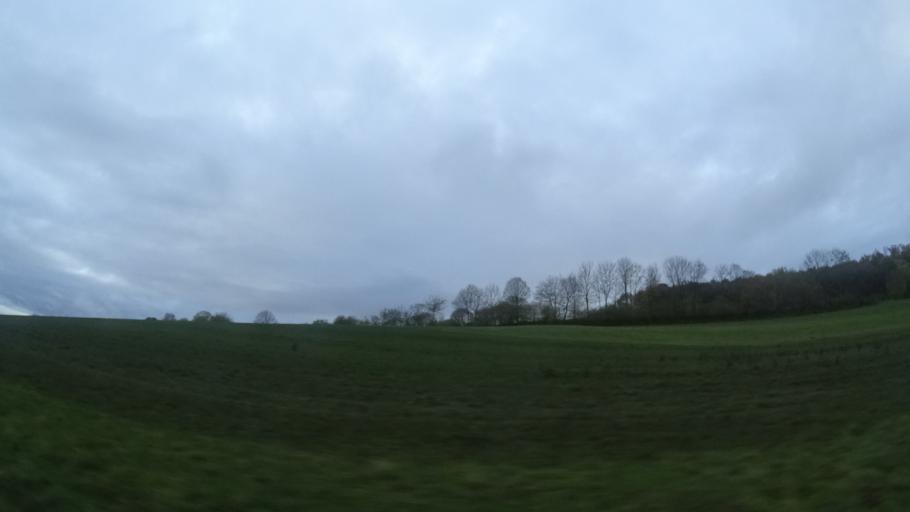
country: DE
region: Hesse
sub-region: Regierungsbezirk Giessen
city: Freiensteinau
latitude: 50.4067
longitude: 9.4217
